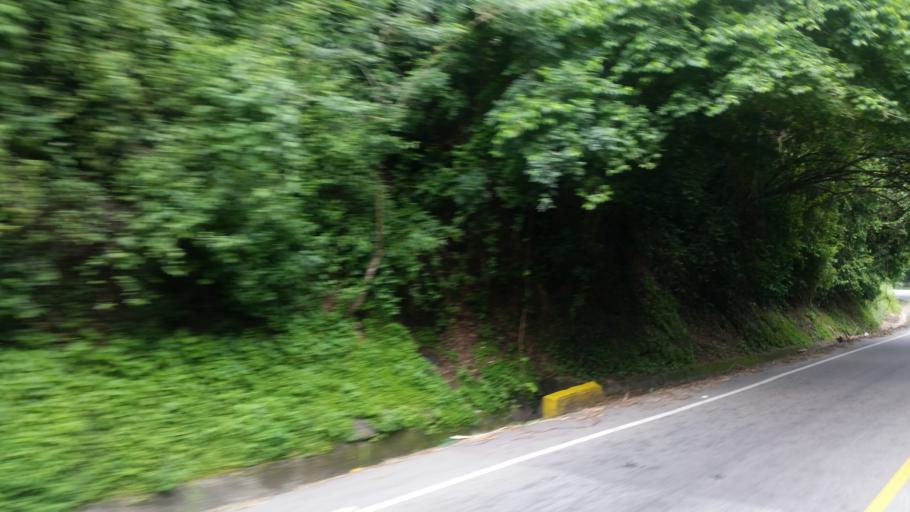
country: CO
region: Magdalena
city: Santa Marta
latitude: 11.2769
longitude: -74.0427
